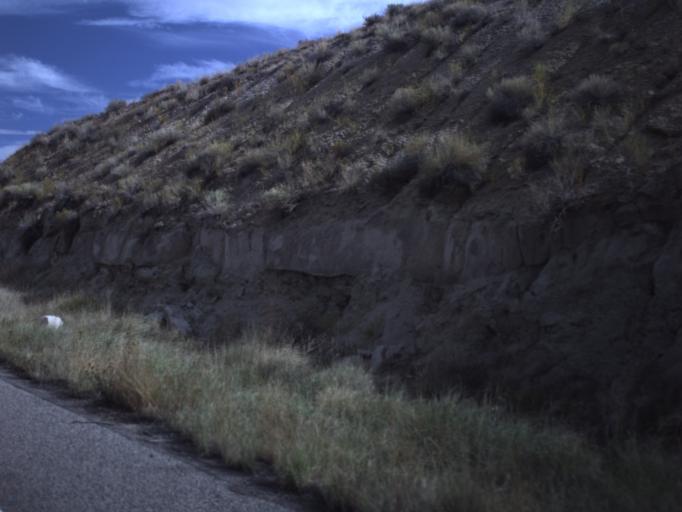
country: US
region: Colorado
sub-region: Montezuma County
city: Towaoc
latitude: 37.1941
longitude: -109.1427
